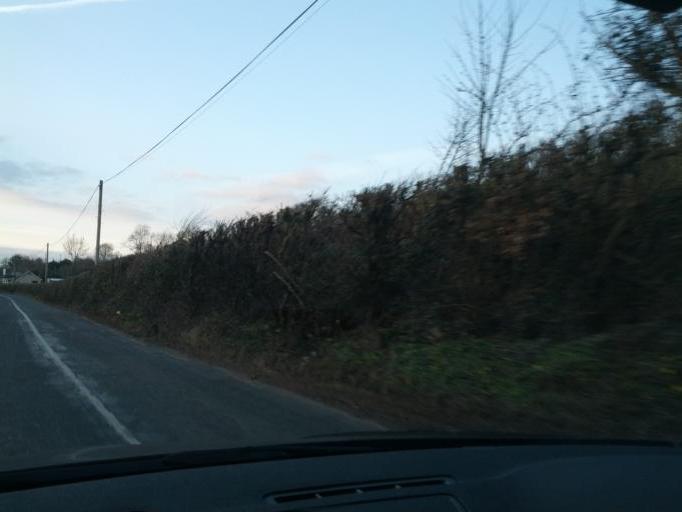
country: IE
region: Munster
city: Nenagh Bridge
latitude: 52.9213
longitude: -8.2225
